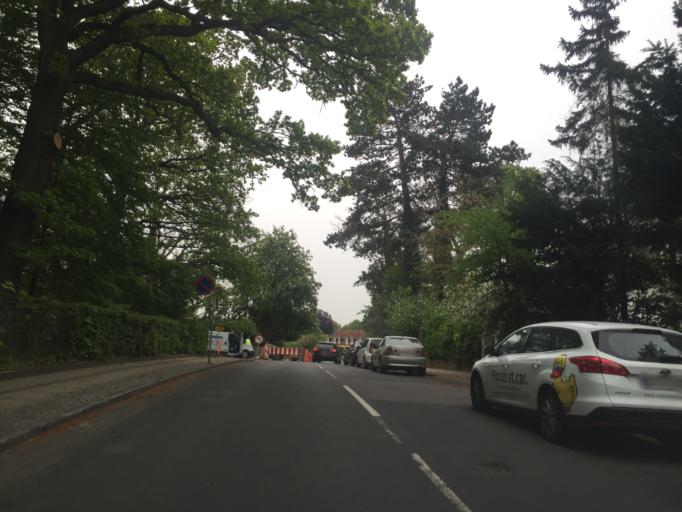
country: DK
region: Capital Region
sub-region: Lyngby-Tarbaek Kommune
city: Kongens Lyngby
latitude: 55.7552
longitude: 12.5440
